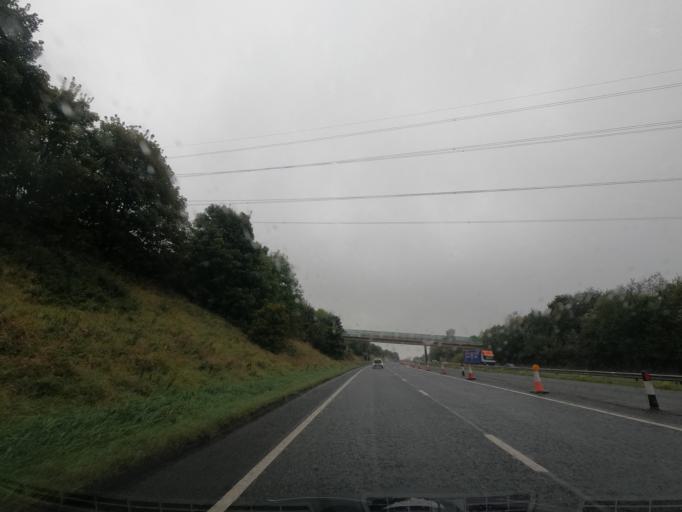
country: GB
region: England
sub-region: Redcar and Cleveland
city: South Bank
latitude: 54.5620
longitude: -1.1265
